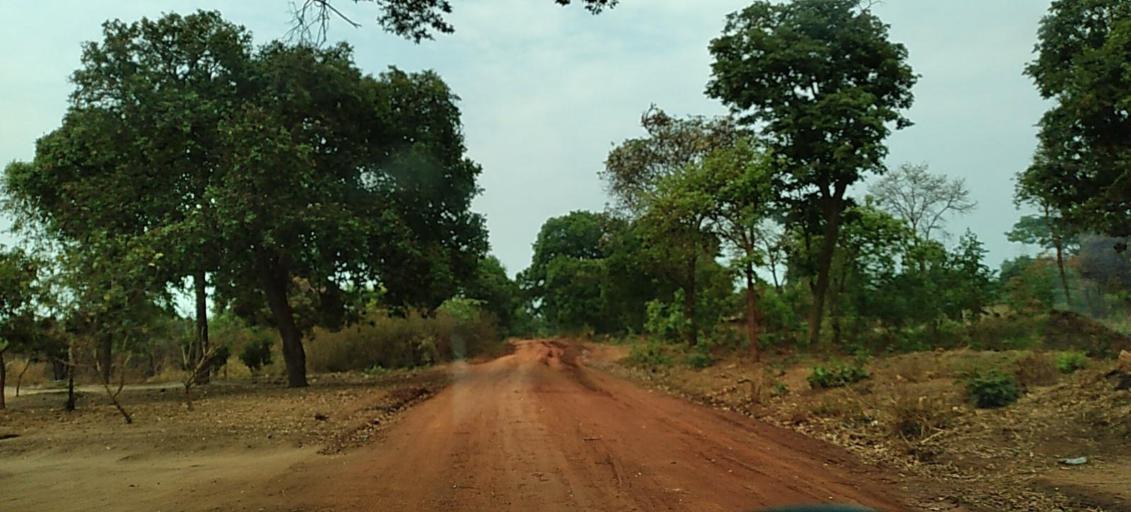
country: ZM
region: North-Western
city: Solwezi
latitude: -12.2471
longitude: 26.5128
